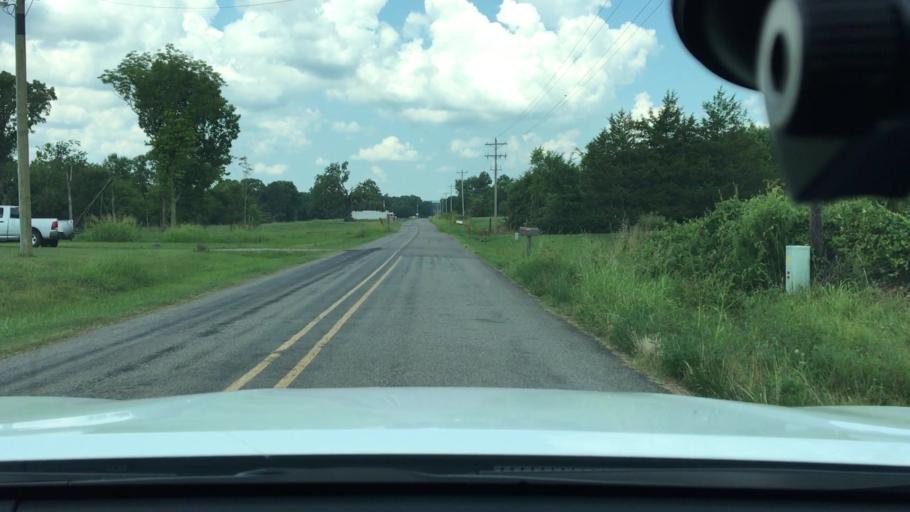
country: US
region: Arkansas
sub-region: Logan County
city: Paris
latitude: 35.2689
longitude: -93.6530
